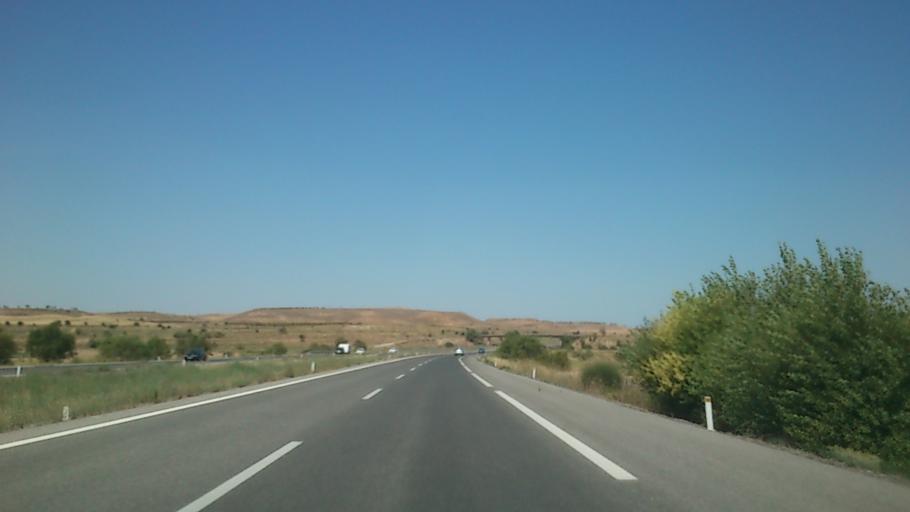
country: ES
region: Navarre
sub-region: Provincia de Navarra
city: Ribaforada
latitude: 41.9562
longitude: -1.5374
